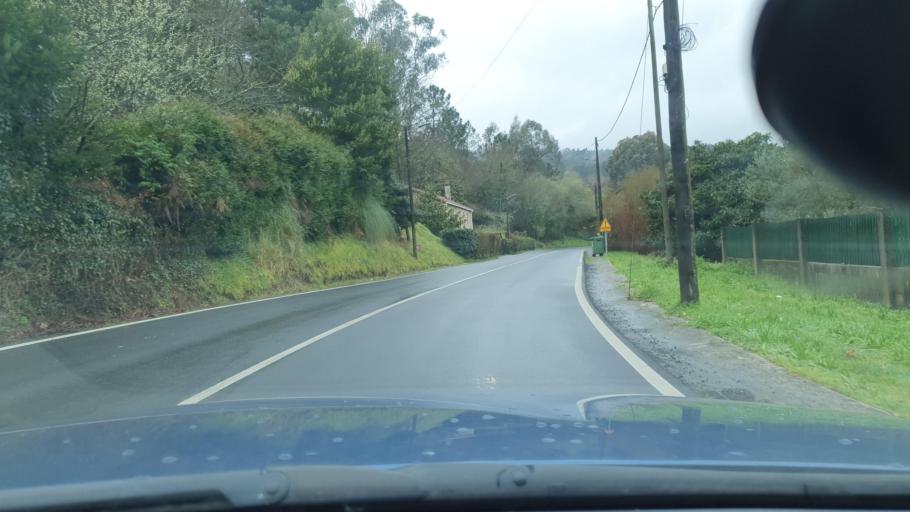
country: ES
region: Galicia
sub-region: Provincia da Coruna
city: Padron
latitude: 42.7499
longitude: -8.6711
